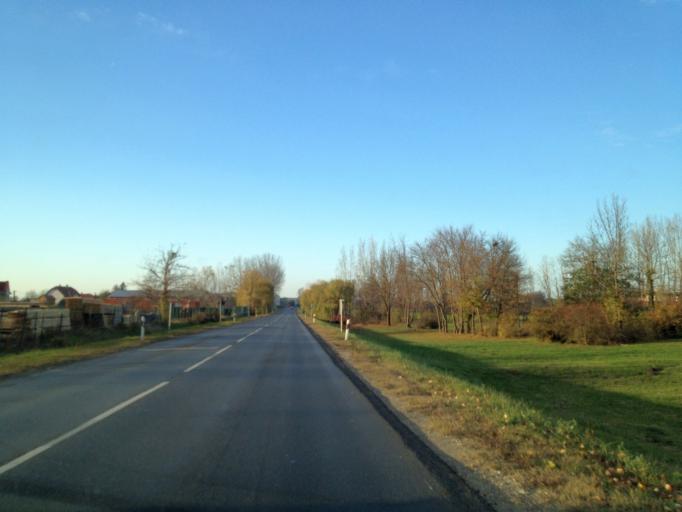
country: HU
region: Gyor-Moson-Sopron
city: Gyorujbarat
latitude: 47.6437
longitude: 17.6625
